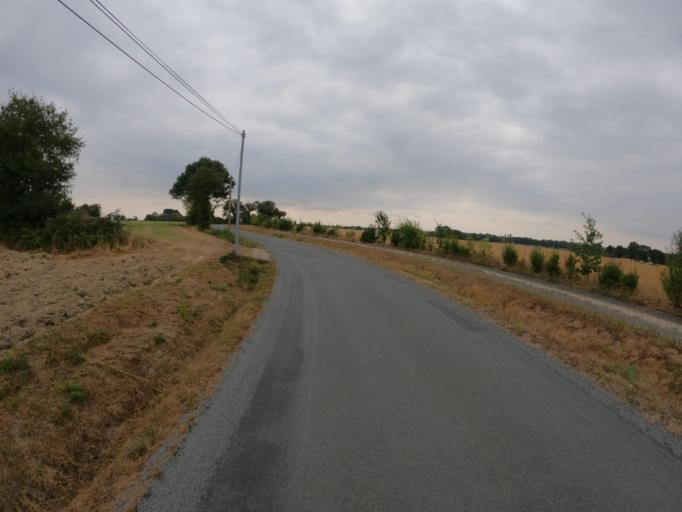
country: FR
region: Pays de la Loire
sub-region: Departement de la Vendee
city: La Guyonniere
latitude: 46.9667
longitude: -1.2661
